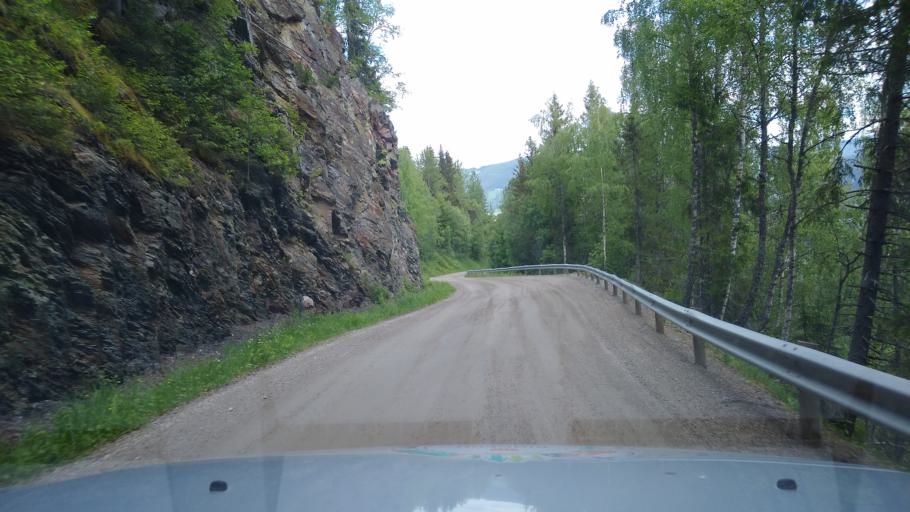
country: NO
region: Oppland
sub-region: Ringebu
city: Ringebu
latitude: 61.5041
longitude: 10.1383
